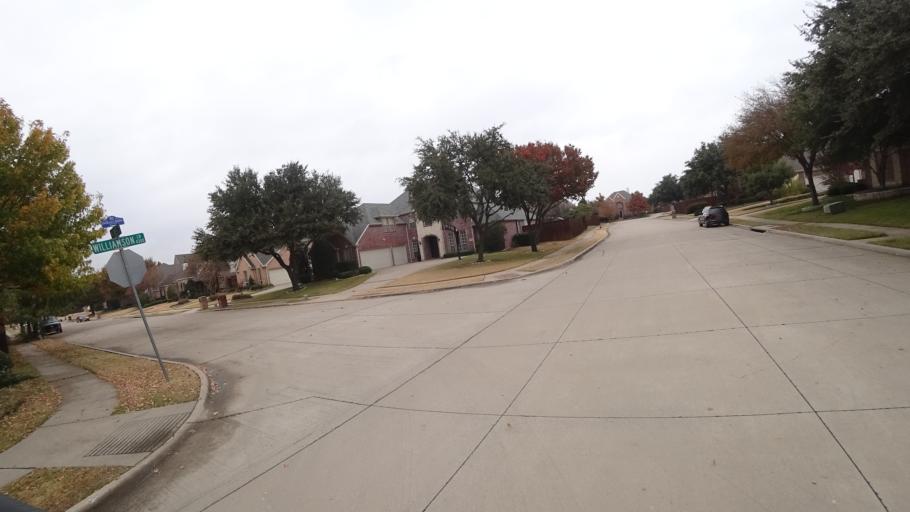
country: US
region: Texas
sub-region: Denton County
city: Lewisville
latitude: 33.0322
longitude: -96.9364
